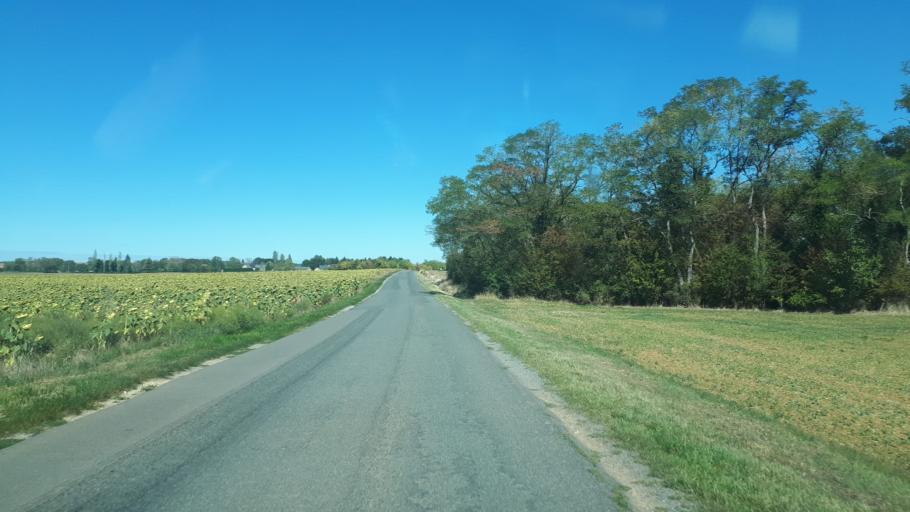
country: FR
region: Centre
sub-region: Departement du Cher
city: Rians
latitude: 47.1901
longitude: 2.7145
